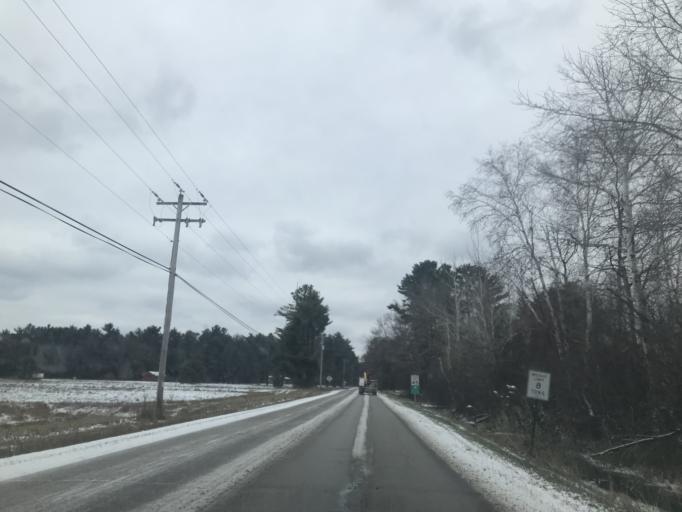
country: US
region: Wisconsin
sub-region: Marinette County
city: Marinette
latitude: 45.0703
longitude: -87.6596
